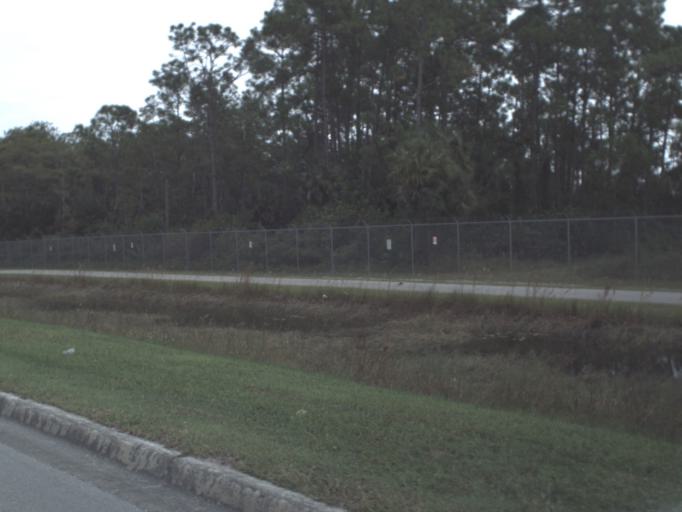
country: US
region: Florida
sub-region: Collier County
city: Lely Resort
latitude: 26.0718
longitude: -81.6925
